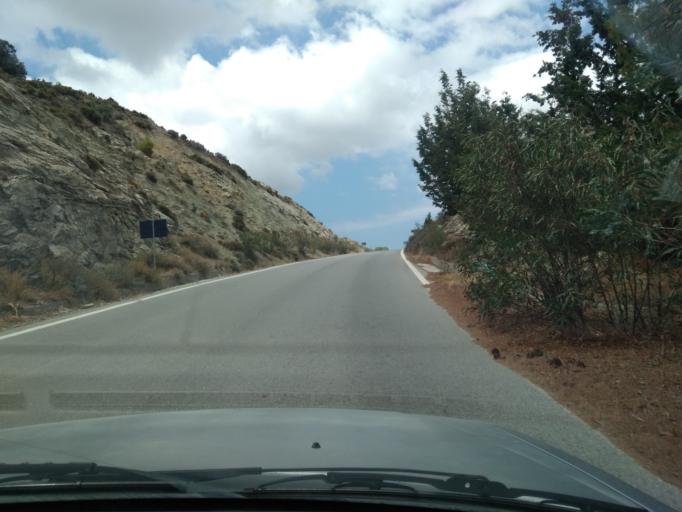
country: GR
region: Crete
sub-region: Nomos Lasithiou
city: Makry-Gialos
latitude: 35.0653
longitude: 26.0468
